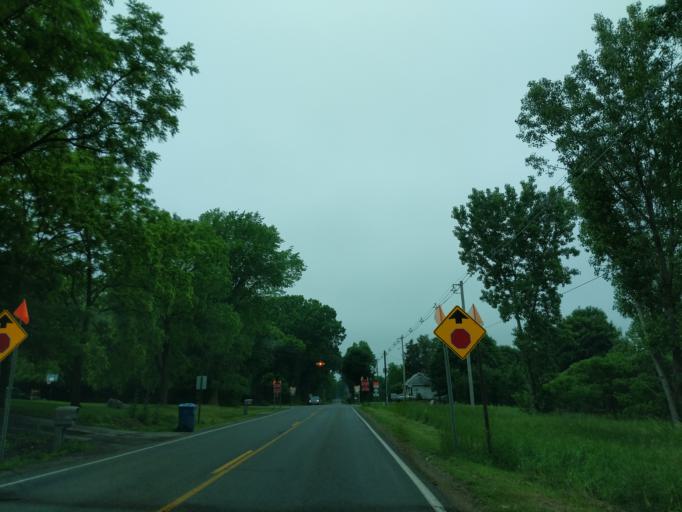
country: US
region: Michigan
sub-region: Jackson County
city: Spring Arbor
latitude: 42.2176
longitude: -84.5410
